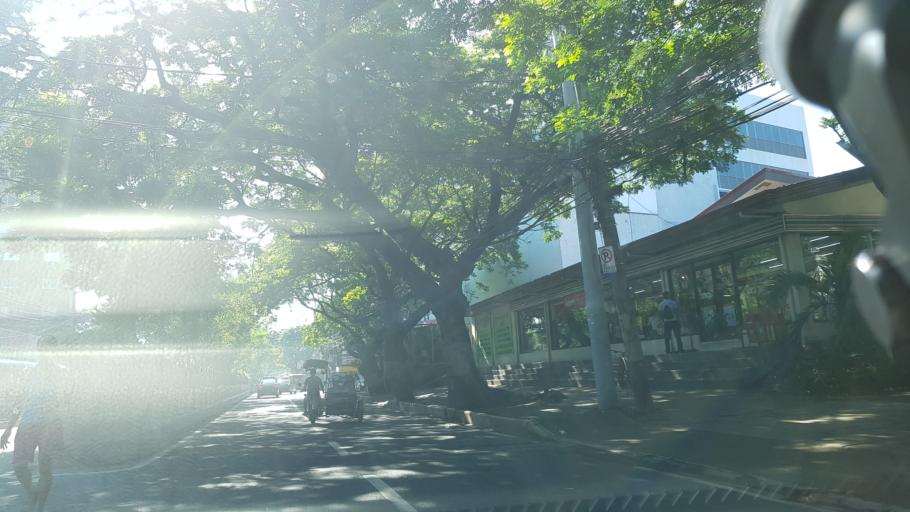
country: PH
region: Metro Manila
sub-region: Pasig
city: Pasig City
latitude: 14.5693
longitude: 121.0840
